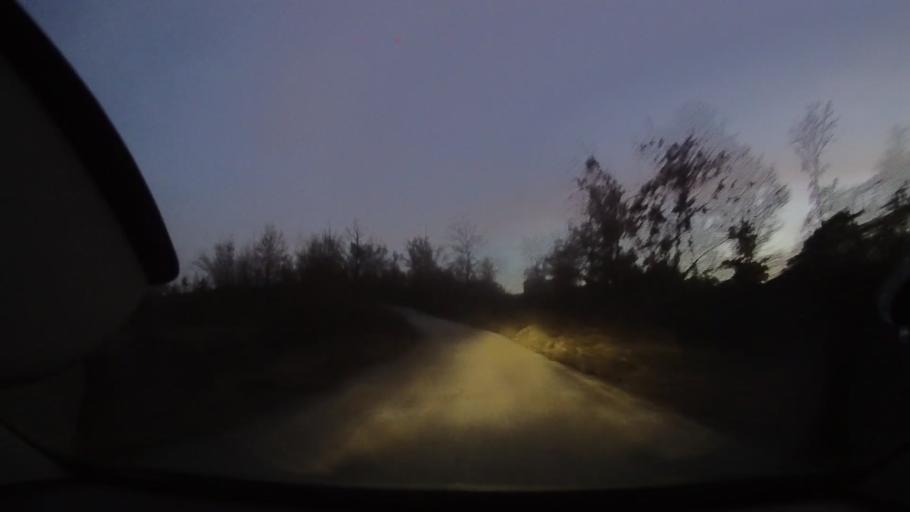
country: RO
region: Bihor
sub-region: Comuna Varciorog
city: Varciorog
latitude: 46.9940
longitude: 22.3096
